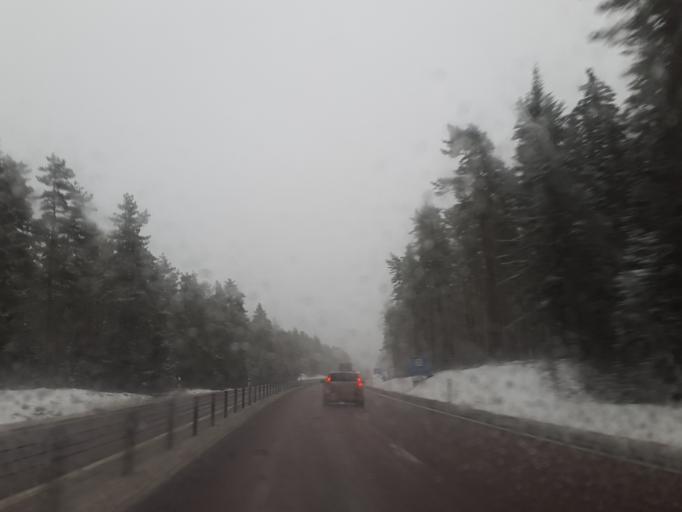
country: SE
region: Joenkoeping
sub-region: Mullsjo Kommun
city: Mullsjoe
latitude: 57.7543
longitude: 13.9091
